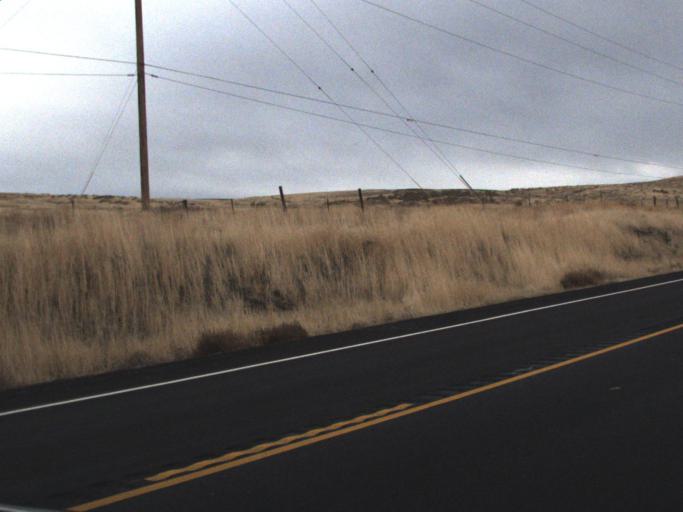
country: US
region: Washington
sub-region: Walla Walla County
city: Burbank
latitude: 46.0692
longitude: -118.7665
